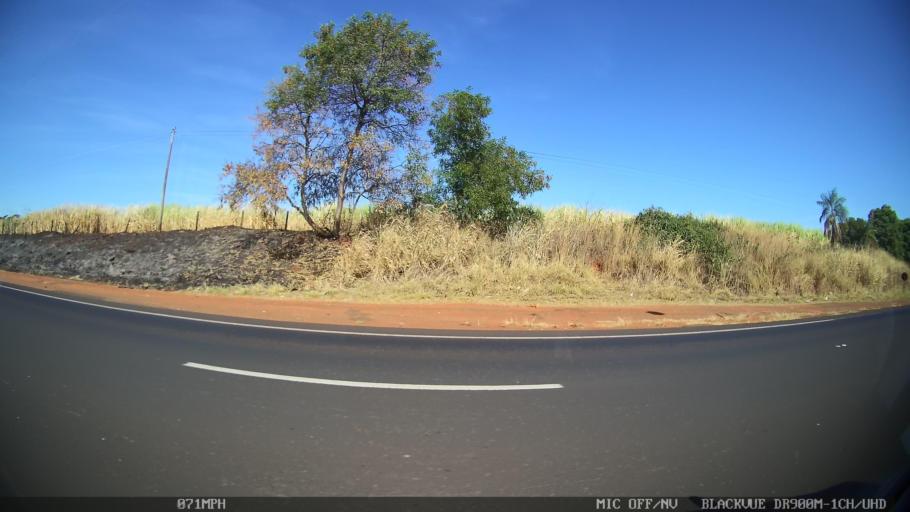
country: BR
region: Sao Paulo
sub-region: Barretos
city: Barretos
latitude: -20.6001
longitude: -48.7254
